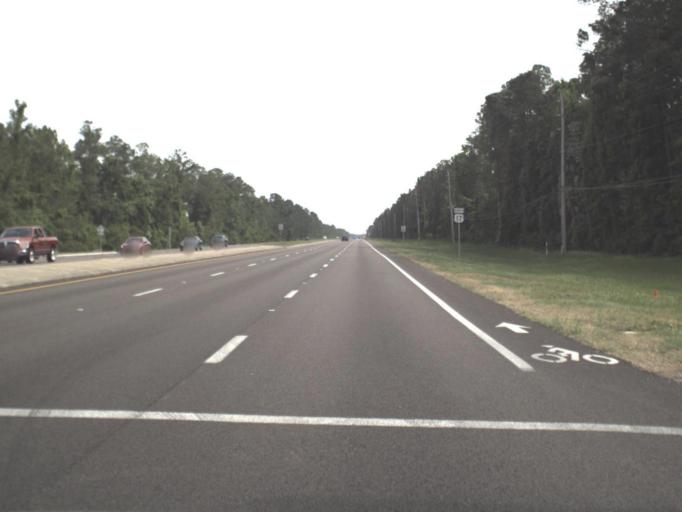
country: US
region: Florida
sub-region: Saint Johns County
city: Fruit Cove
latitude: 30.0799
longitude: -81.7066
